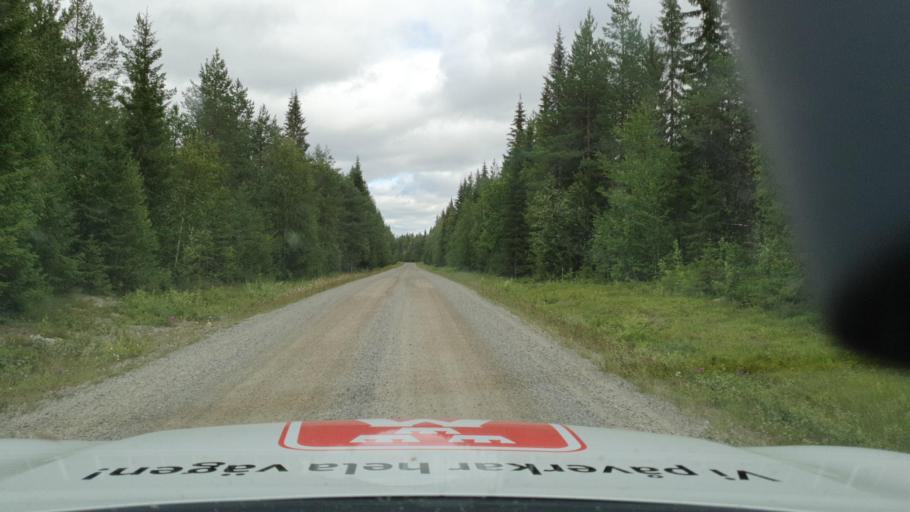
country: SE
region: Vaesterbotten
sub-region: Dorotea Kommun
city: Dorotea
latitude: 64.2047
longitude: 16.8365
